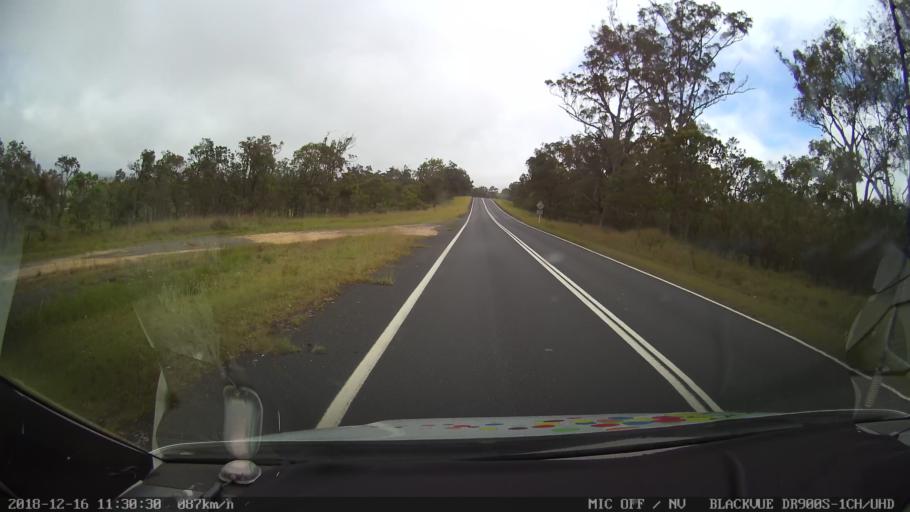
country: AU
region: New South Wales
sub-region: Tenterfield Municipality
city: Carrolls Creek
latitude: -29.0319
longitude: 152.1208
